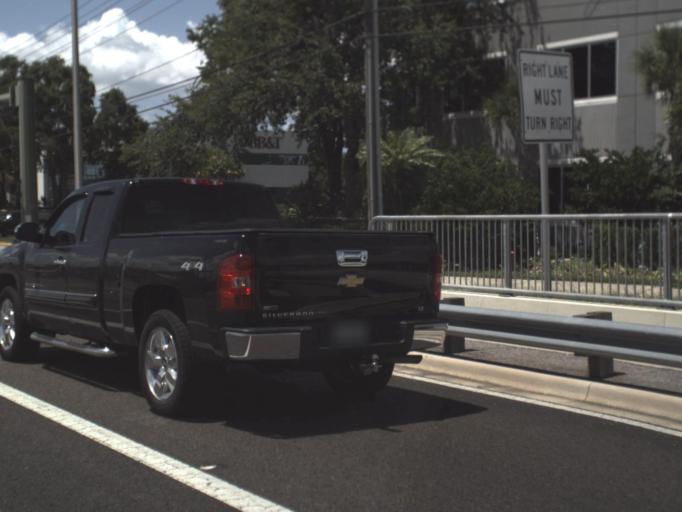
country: US
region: Florida
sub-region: Pinellas County
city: South Highpoint
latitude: 27.8940
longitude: -82.7120
